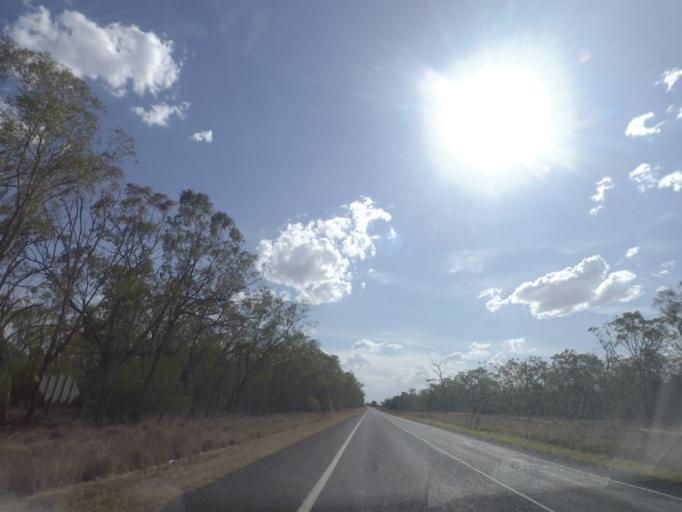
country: AU
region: New South Wales
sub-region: Moree Plains
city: Boggabilla
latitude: -28.5459
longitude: 150.8774
